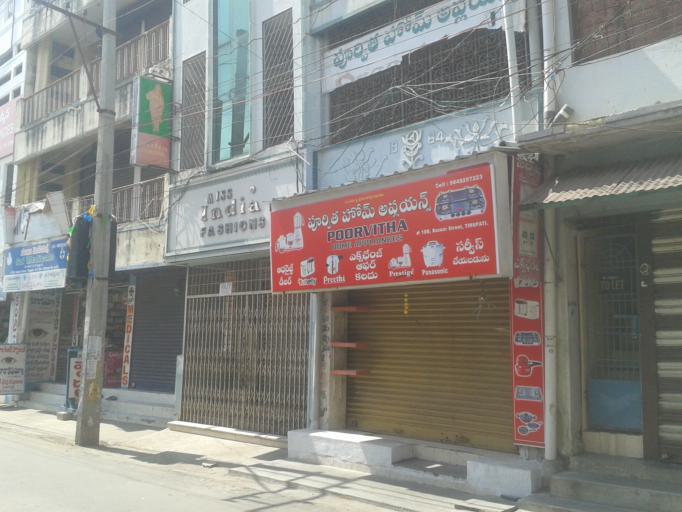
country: IN
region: Andhra Pradesh
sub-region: Chittoor
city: Tirupati
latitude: 13.6344
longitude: 79.4156
